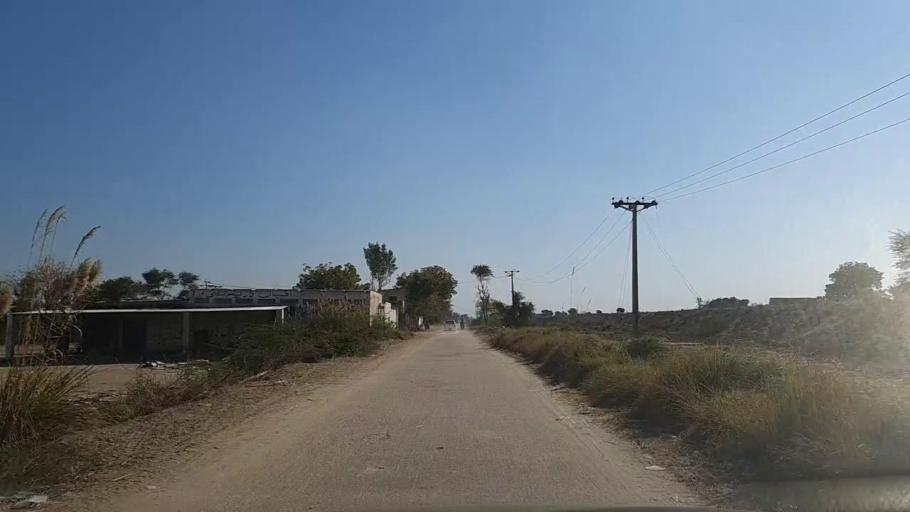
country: PK
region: Sindh
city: Nawabshah
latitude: 26.2396
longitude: 68.4241
